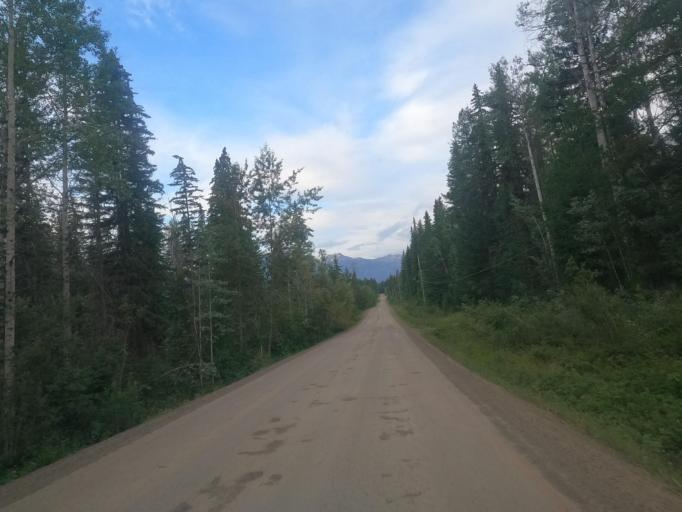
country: CA
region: British Columbia
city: Golden
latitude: 51.4384
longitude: -117.0461
